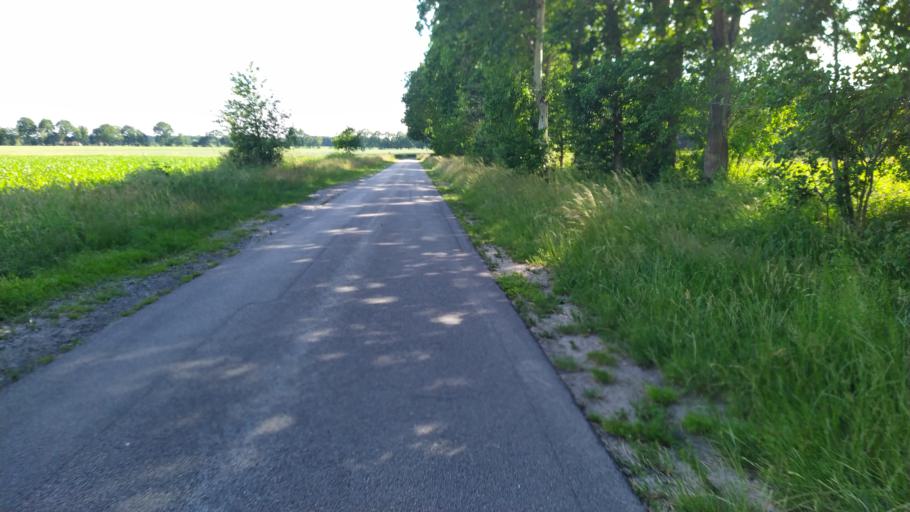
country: DE
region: Lower Saxony
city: Lintig
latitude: 53.6402
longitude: 8.9027
